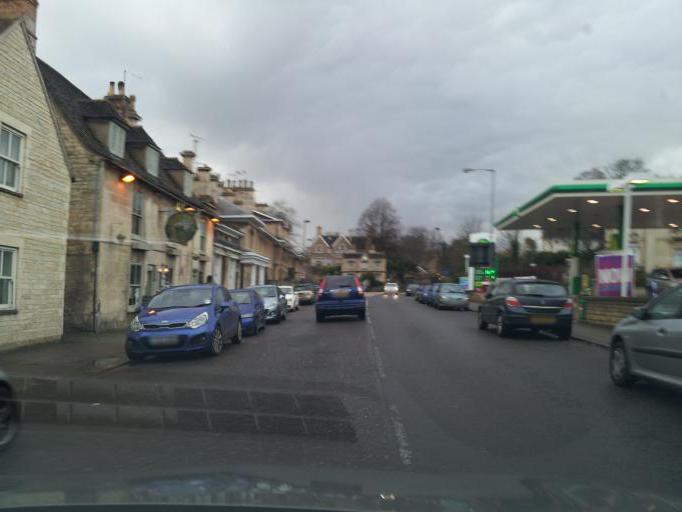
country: GB
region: England
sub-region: Lincolnshire
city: Stamford
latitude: 52.6531
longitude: -0.4851
